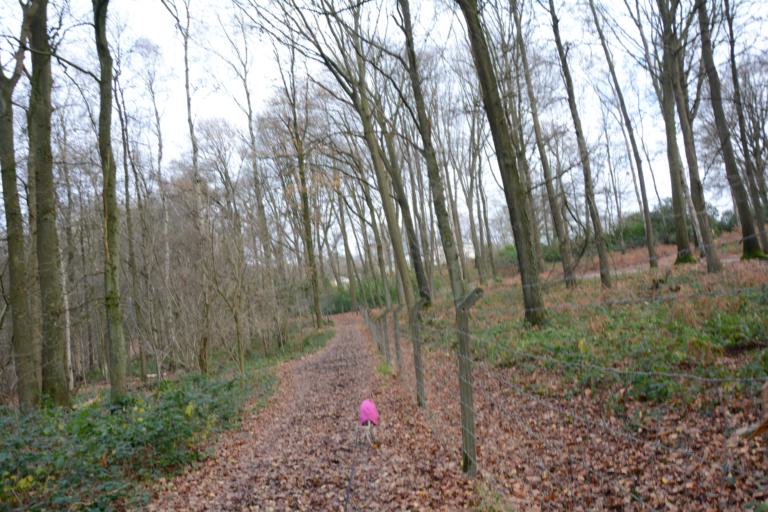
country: BE
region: Flanders
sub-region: Provincie Vlaams-Brabant
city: Asse
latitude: 50.9297
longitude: 4.1571
